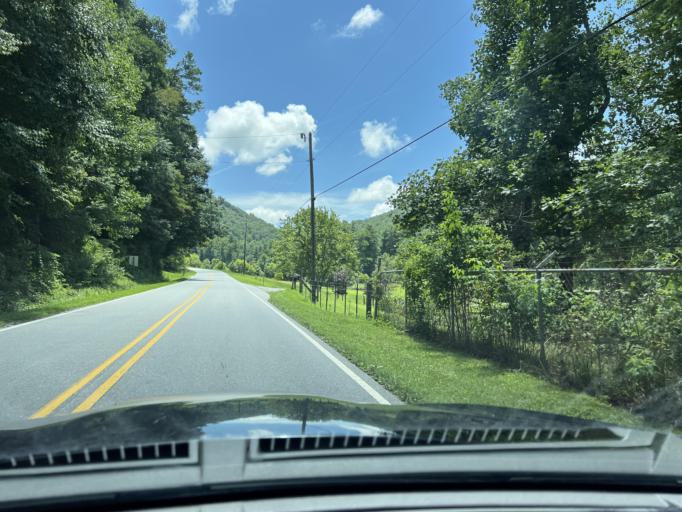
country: US
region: North Carolina
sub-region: Henderson County
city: Hoopers Creek
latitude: 35.4295
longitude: -82.4248
